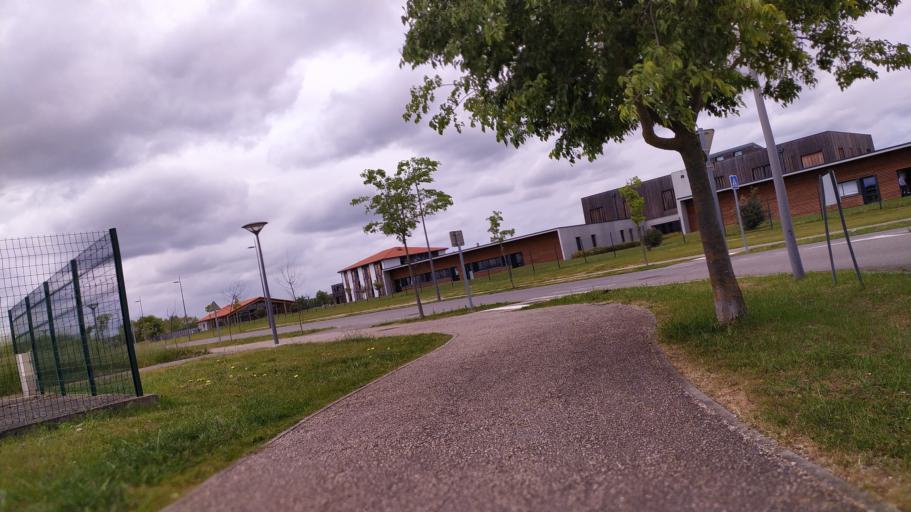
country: FR
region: Midi-Pyrenees
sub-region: Departement de la Haute-Garonne
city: La Salvetat-Saint-Gilles
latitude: 43.5839
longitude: 1.2852
